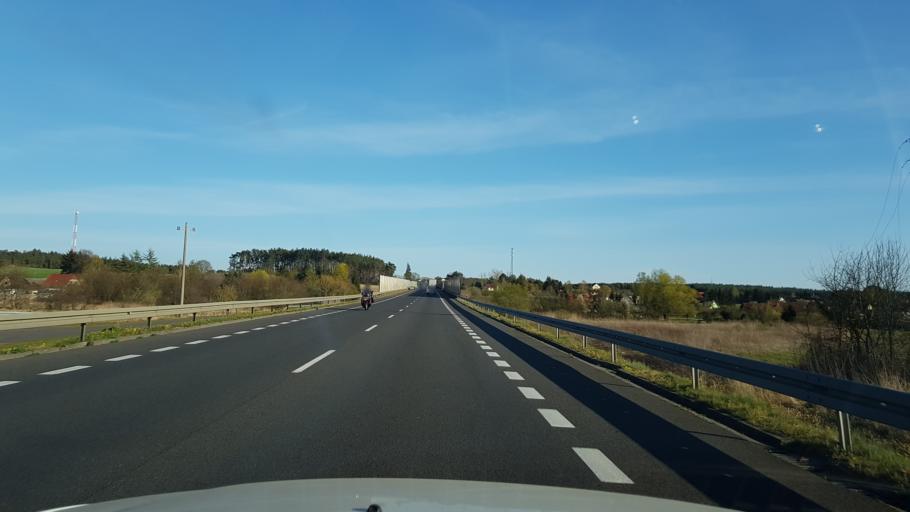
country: PL
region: West Pomeranian Voivodeship
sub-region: Powiat kamienski
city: Wolin
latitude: 53.8741
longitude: 14.5378
